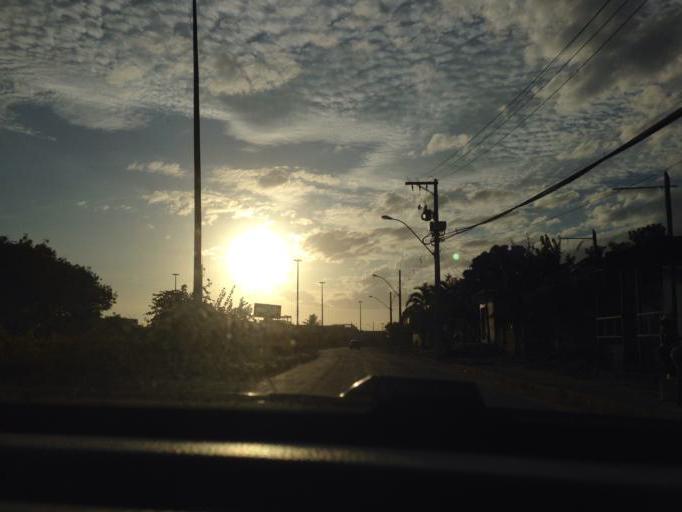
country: BR
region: Espirito Santo
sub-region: Guarapari
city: Guarapari
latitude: -20.6252
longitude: -40.4372
